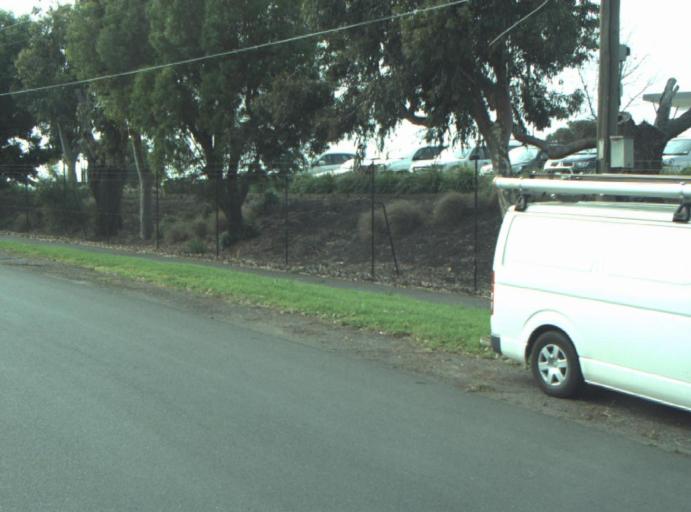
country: AU
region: Victoria
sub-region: Greater Geelong
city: Bell Park
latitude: -38.1002
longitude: 144.3704
